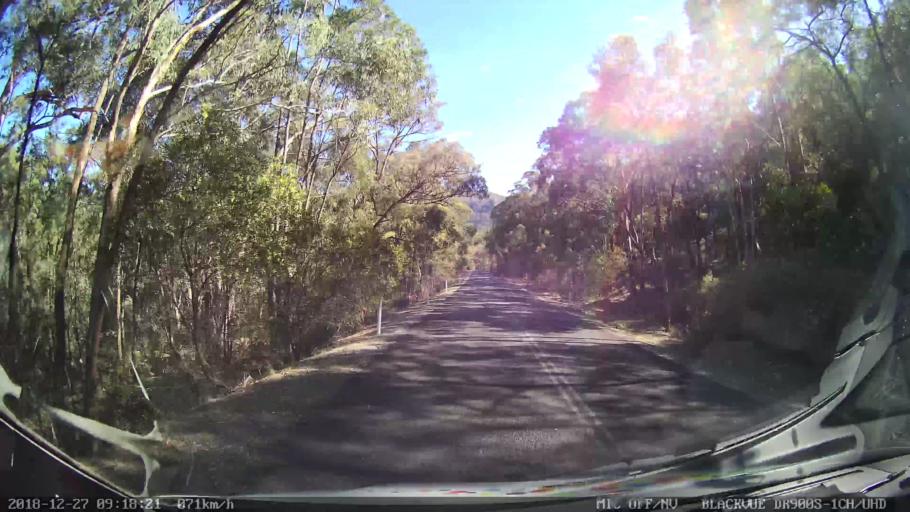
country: AU
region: New South Wales
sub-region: Lithgow
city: Portland
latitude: -33.1279
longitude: 150.0449
